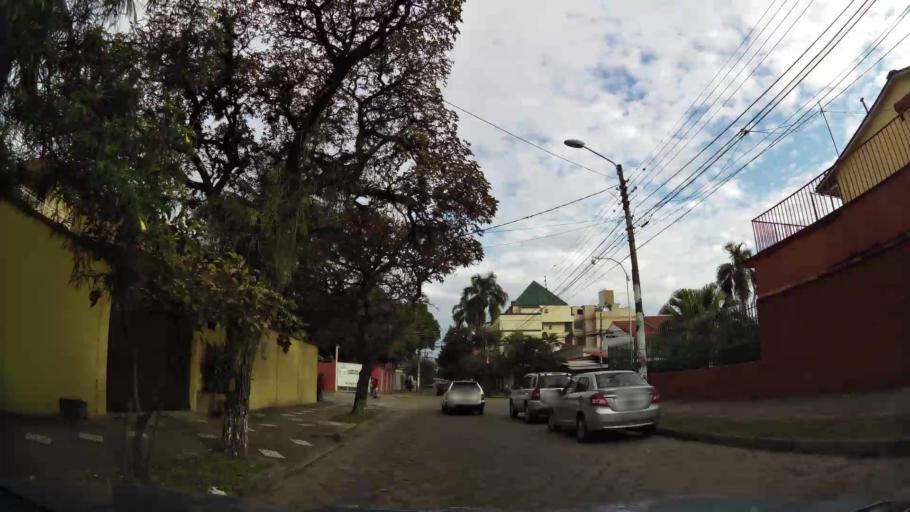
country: BO
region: Santa Cruz
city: Santa Cruz de la Sierra
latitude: -17.7889
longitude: -63.1724
